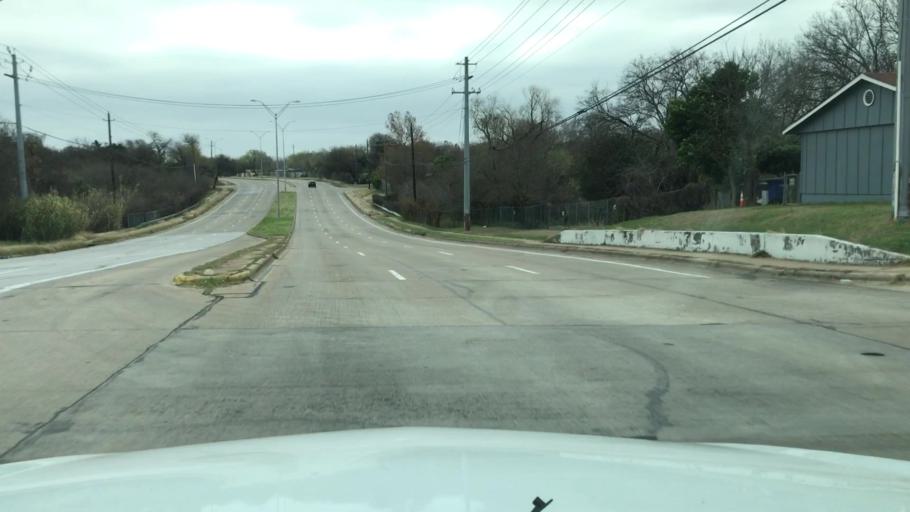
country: US
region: Texas
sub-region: Travis County
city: Onion Creek
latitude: 30.1829
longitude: -97.7536
